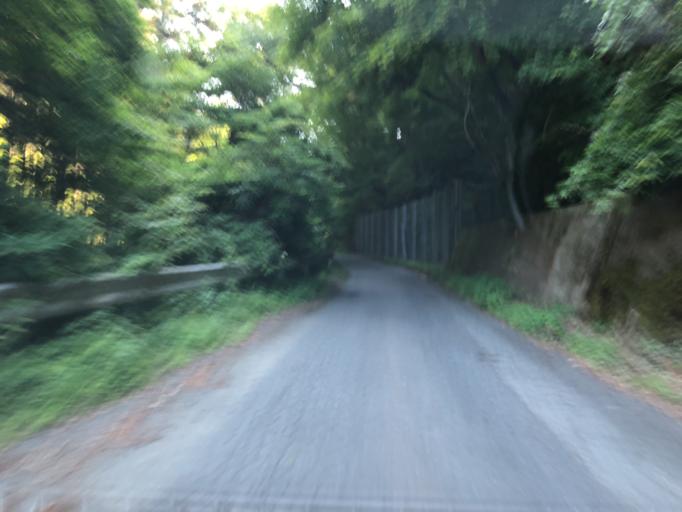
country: JP
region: Ibaraki
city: Kitaibaraki
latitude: 36.8668
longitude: 140.6957
